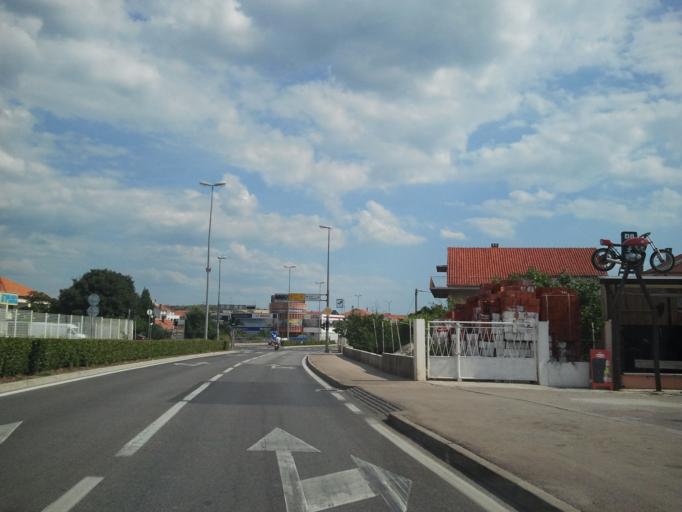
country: HR
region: Zadarska
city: Zadar
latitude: 44.1100
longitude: 15.2586
